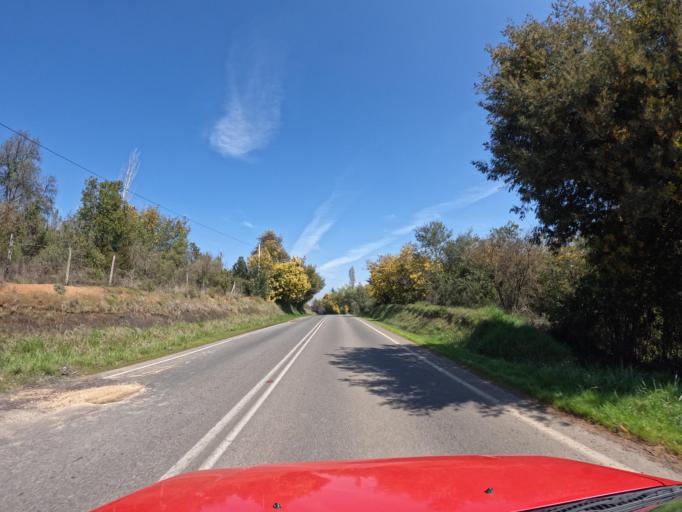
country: CL
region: Maule
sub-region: Provincia de Talca
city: San Clemente
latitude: -35.4813
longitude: -71.2700
